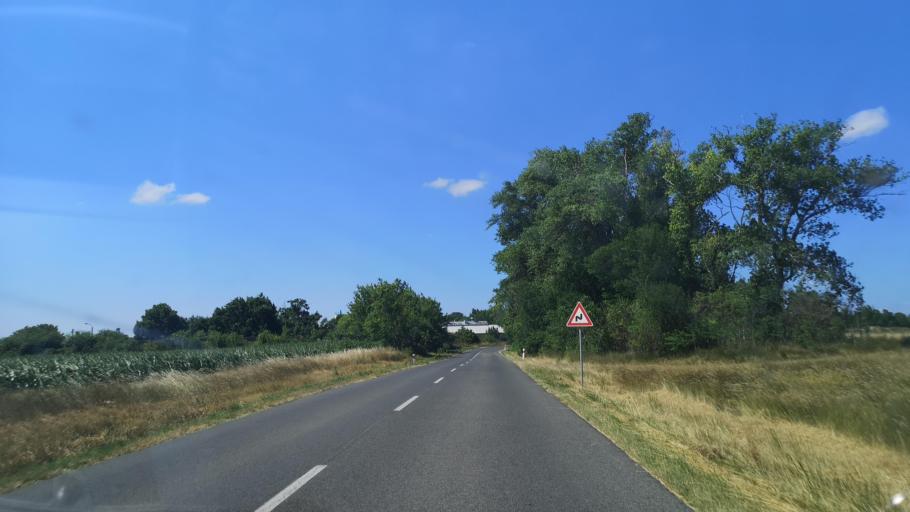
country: SK
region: Trnavsky
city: Dunajska Streda
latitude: 48.0602
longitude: 17.4702
